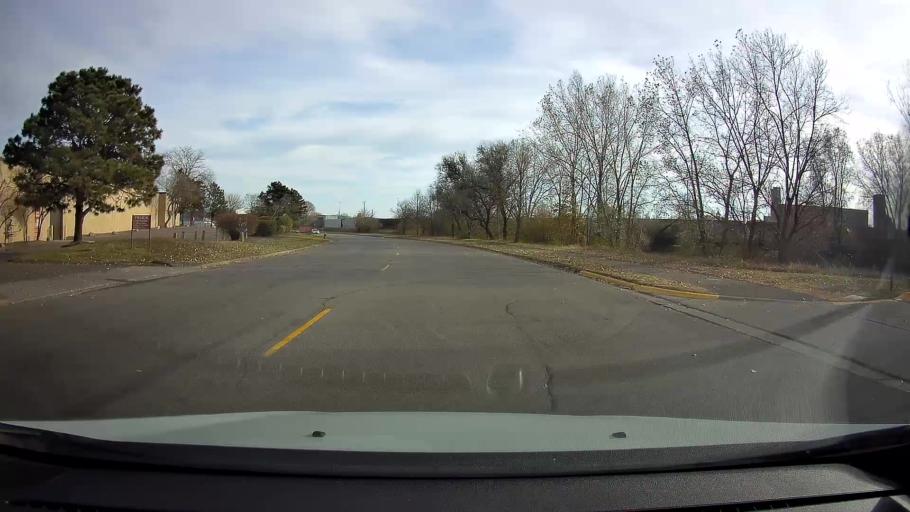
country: US
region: Minnesota
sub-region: Ramsey County
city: Lauderdale
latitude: 44.9795
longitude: -93.2128
